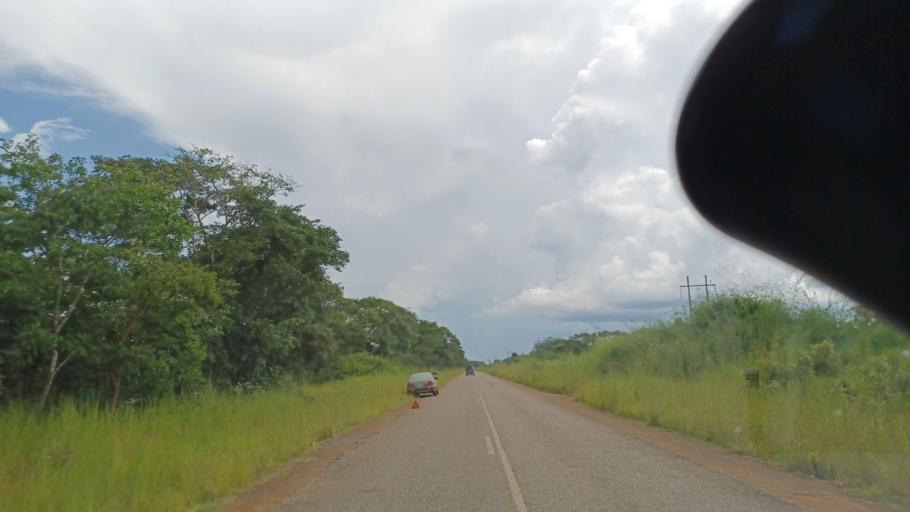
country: ZM
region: North-Western
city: Kasempa
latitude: -13.1349
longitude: 25.8770
